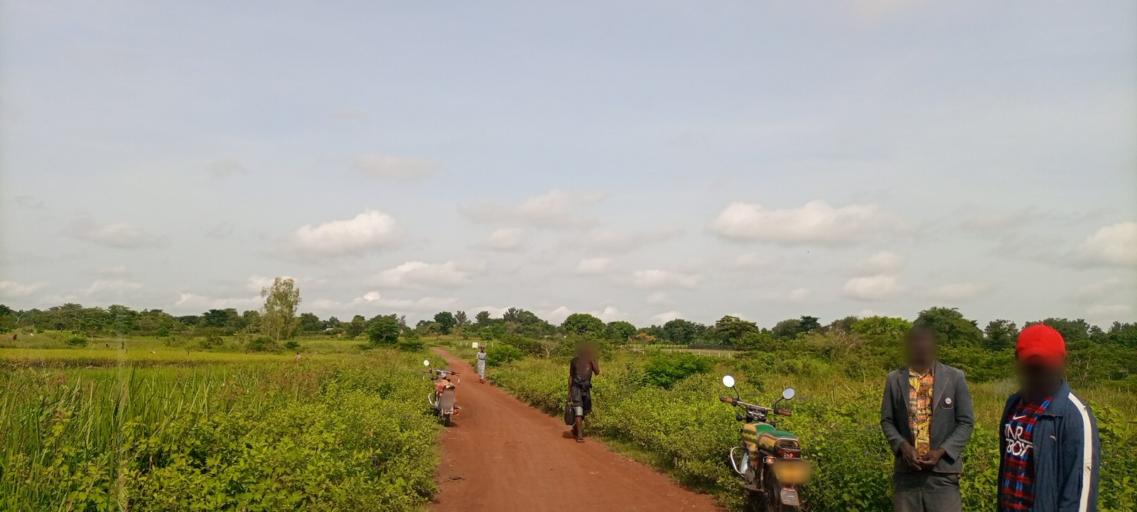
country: UG
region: Eastern Region
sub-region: Kibuku District
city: Kibuku
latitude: 1.0972
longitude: 33.7699
